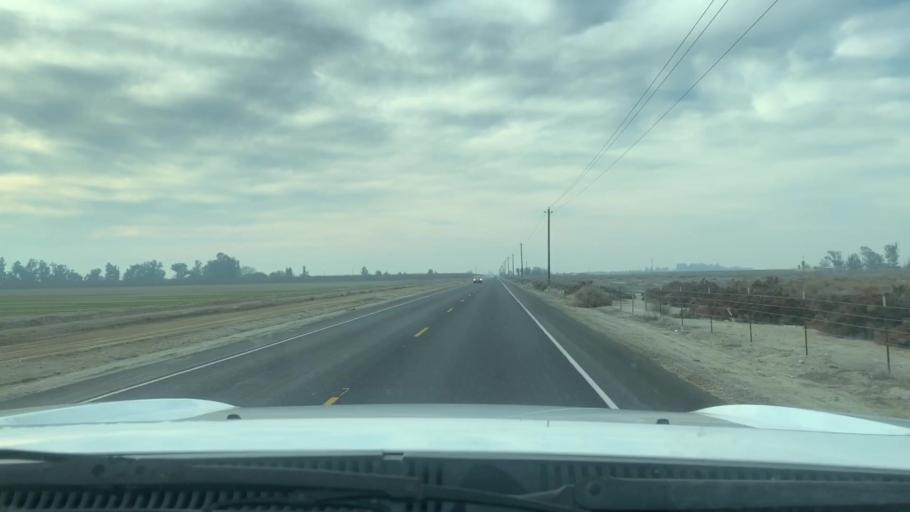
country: US
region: California
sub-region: Kern County
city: Buttonwillow
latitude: 35.4422
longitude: -119.3978
